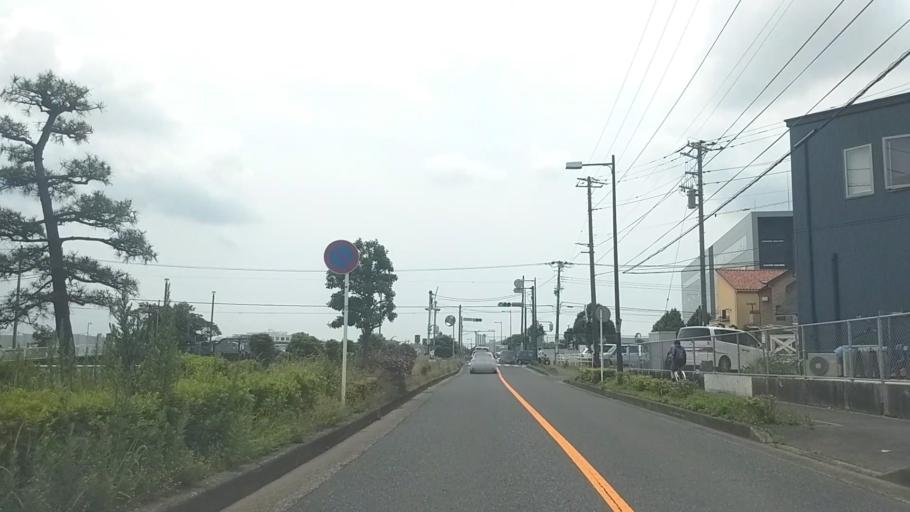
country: JP
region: Kanagawa
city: Fujisawa
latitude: 35.3428
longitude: 139.4665
